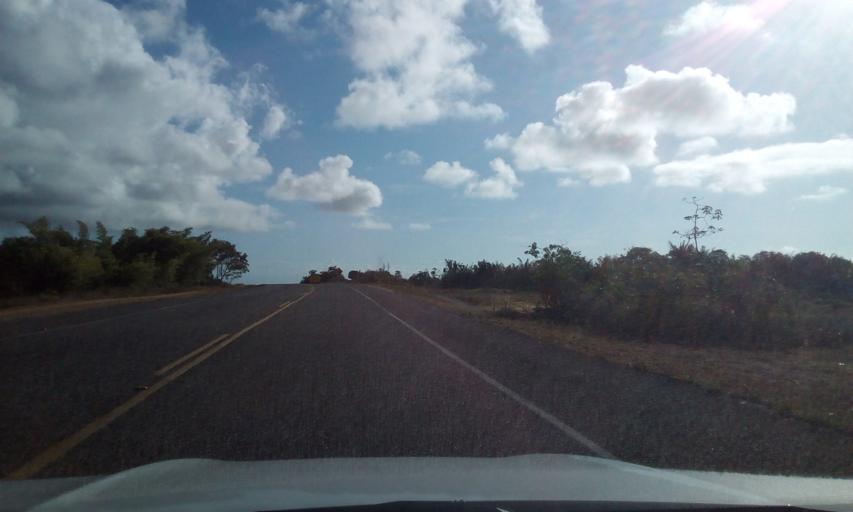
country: BR
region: Bahia
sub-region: Conde
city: Conde
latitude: -12.0806
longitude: -37.7625
